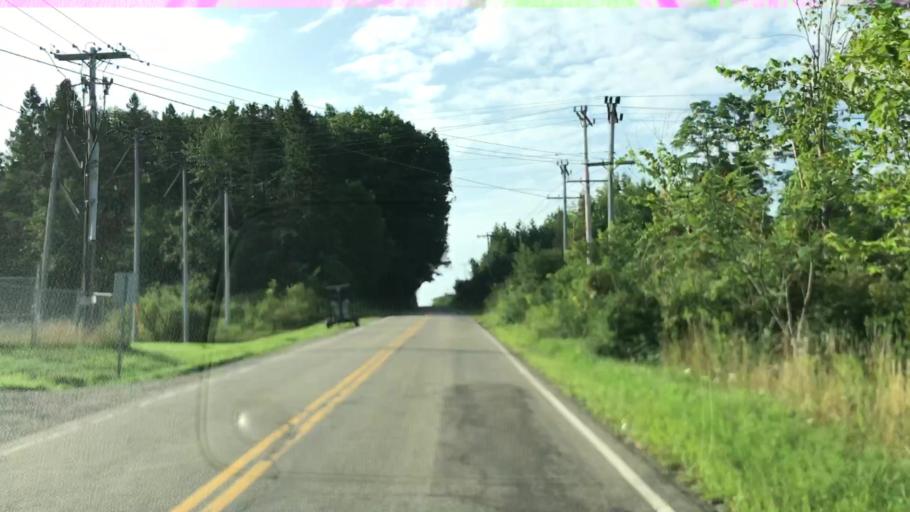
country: US
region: New York
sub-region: Chautauqua County
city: Mayville
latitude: 42.2618
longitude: -79.4701
